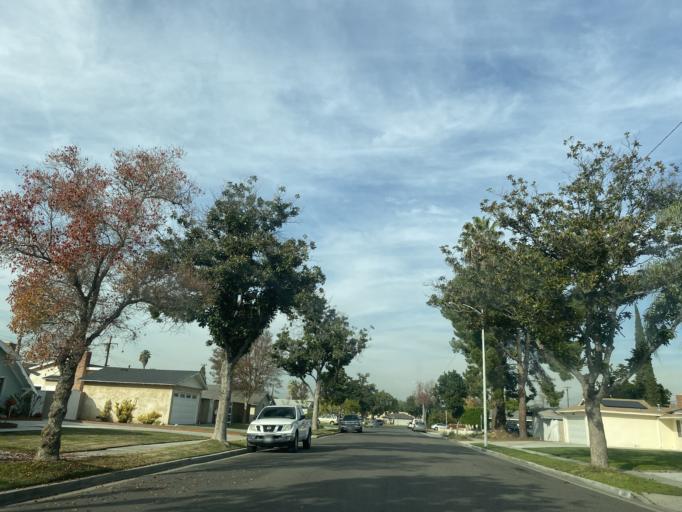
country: US
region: California
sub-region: Orange County
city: Fullerton
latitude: 33.8514
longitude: -117.9610
